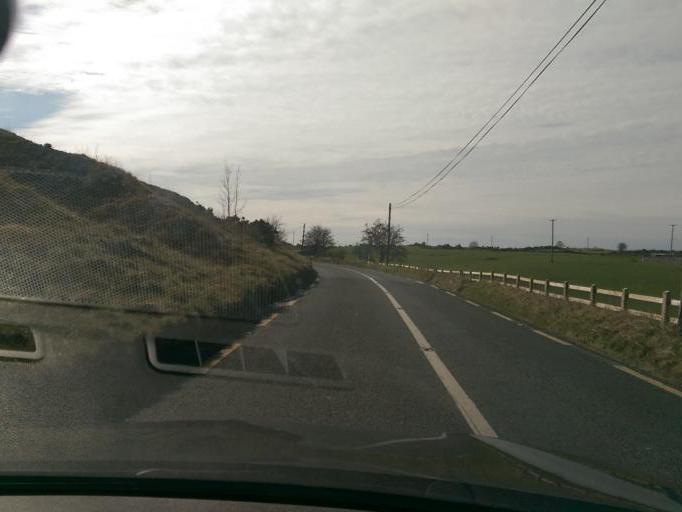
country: IE
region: Connaught
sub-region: County Galway
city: Athenry
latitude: 53.4657
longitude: -8.6673
